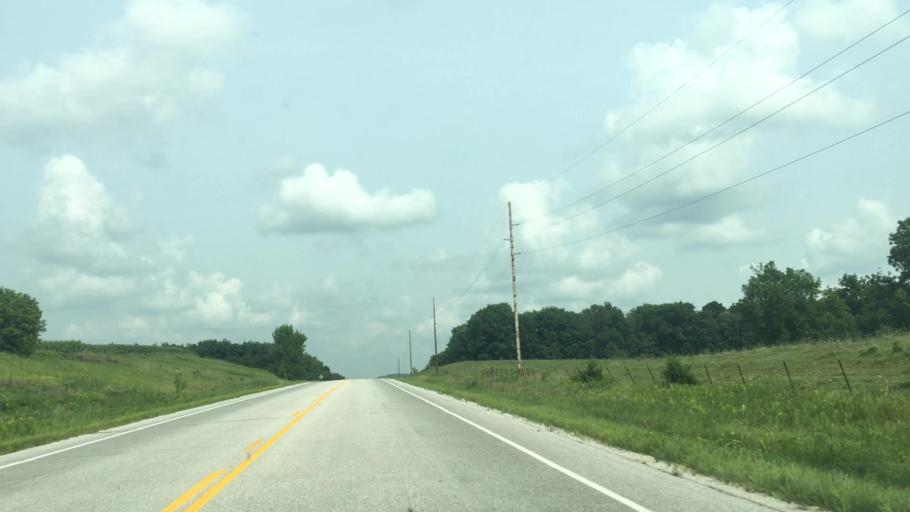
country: US
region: Minnesota
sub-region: Fillmore County
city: Harmony
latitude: 43.5842
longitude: -91.9298
